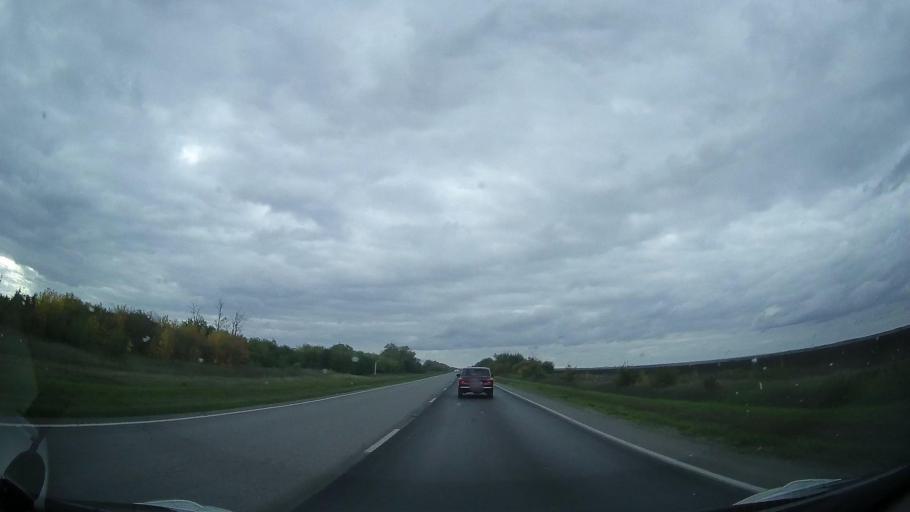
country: RU
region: Rostov
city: Yegorlykskaya
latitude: 46.5460
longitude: 40.7614
